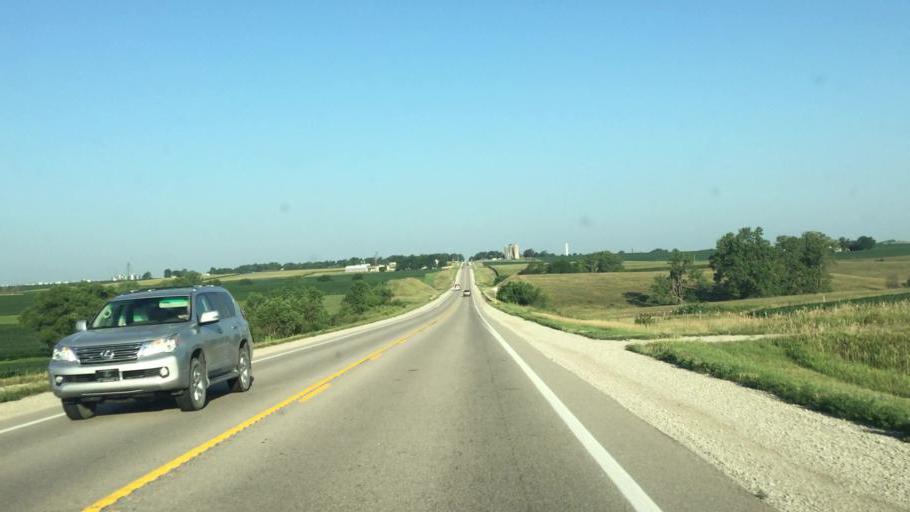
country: US
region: Kansas
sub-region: Nemaha County
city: Sabetha
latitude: 39.8411
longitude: -95.7021
